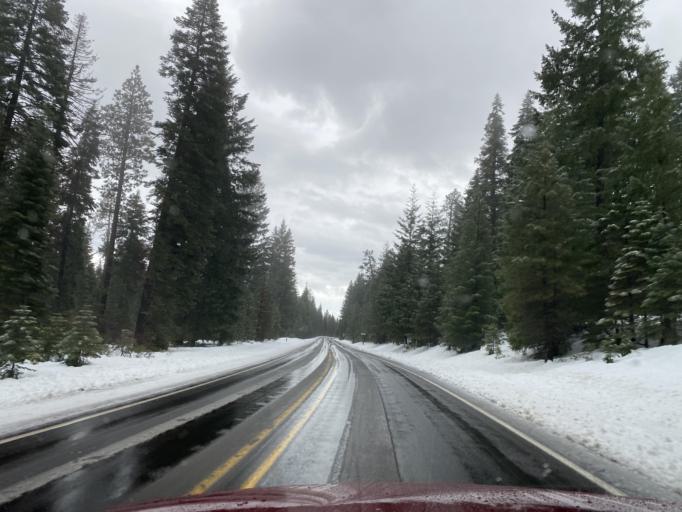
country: US
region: Oregon
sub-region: Klamath County
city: Klamath Falls
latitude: 42.5253
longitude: -122.0882
